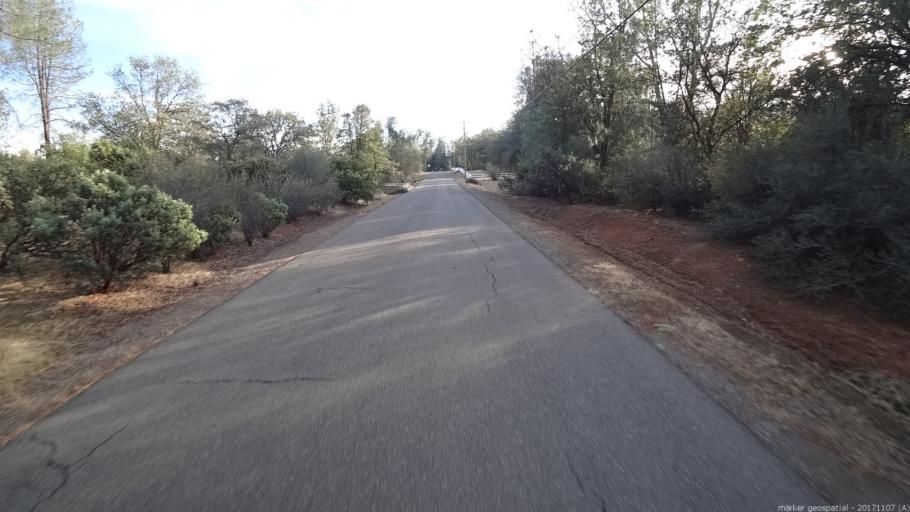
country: US
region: California
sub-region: Shasta County
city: Shasta
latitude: 40.5284
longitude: -122.4826
